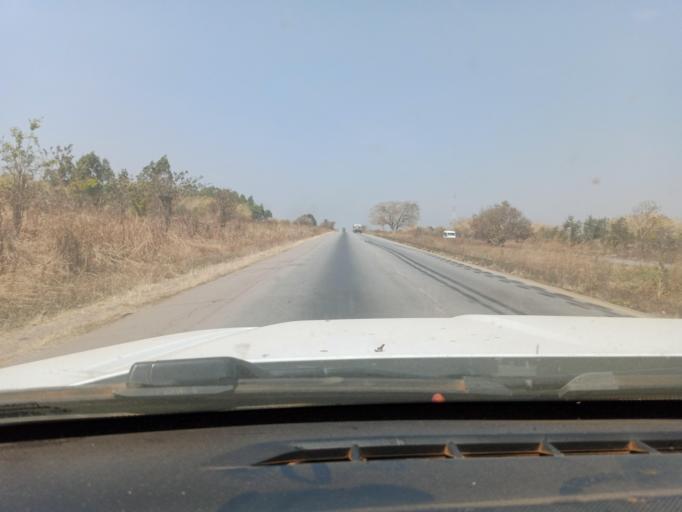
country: ZM
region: Copperbelt
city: Luanshya
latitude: -12.9928
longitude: 28.4174
